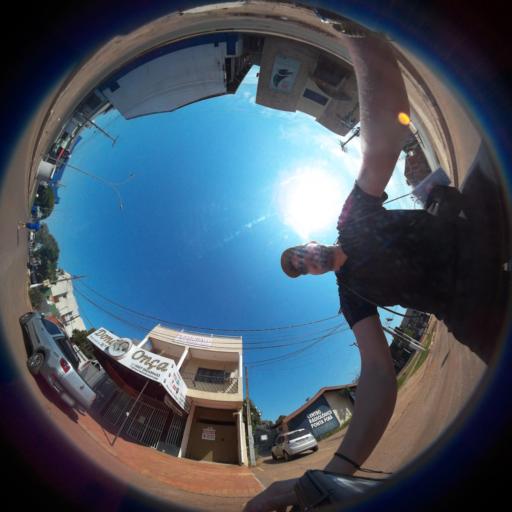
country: BR
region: Mato Grosso do Sul
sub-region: Ponta Pora
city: Ponta Pora
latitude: -22.5365
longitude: -55.7271
